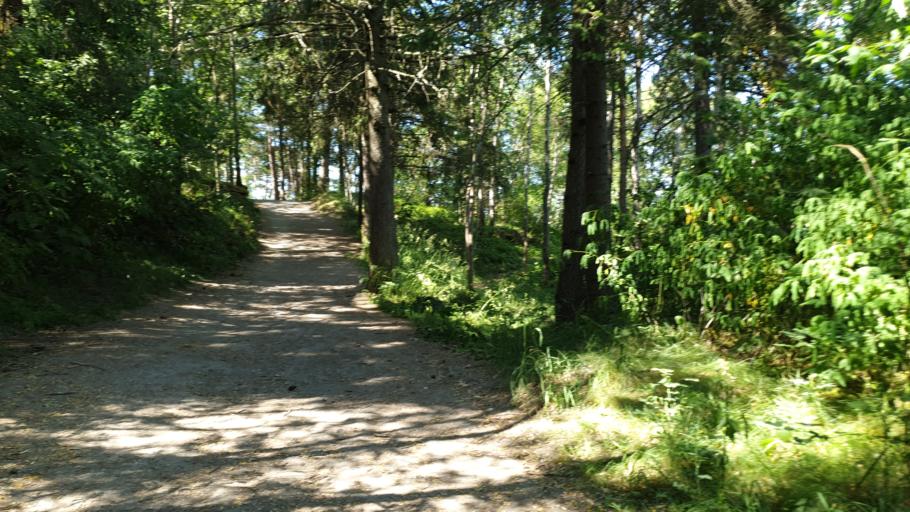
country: NO
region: Sor-Trondelag
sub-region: Trondheim
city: Trondheim
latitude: 63.4420
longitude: 10.4856
